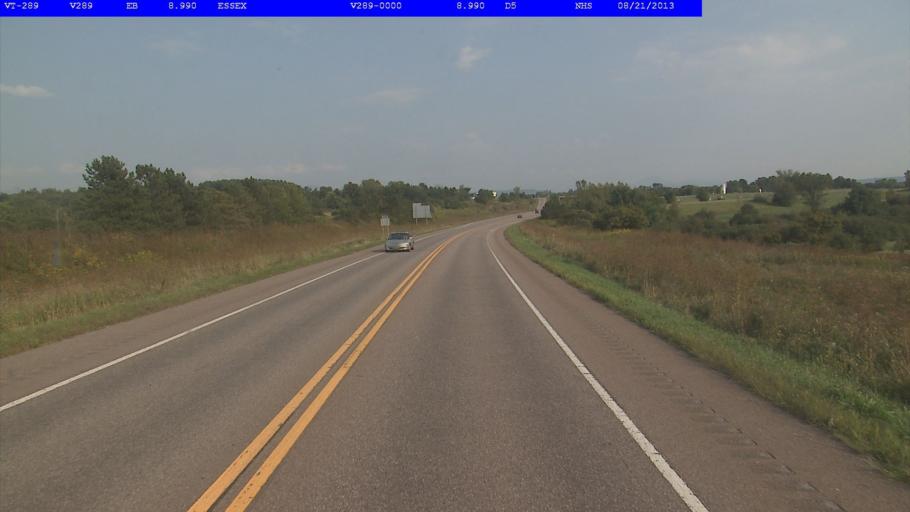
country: US
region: Vermont
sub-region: Chittenden County
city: Essex Junction
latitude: 44.5119
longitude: -73.0951
